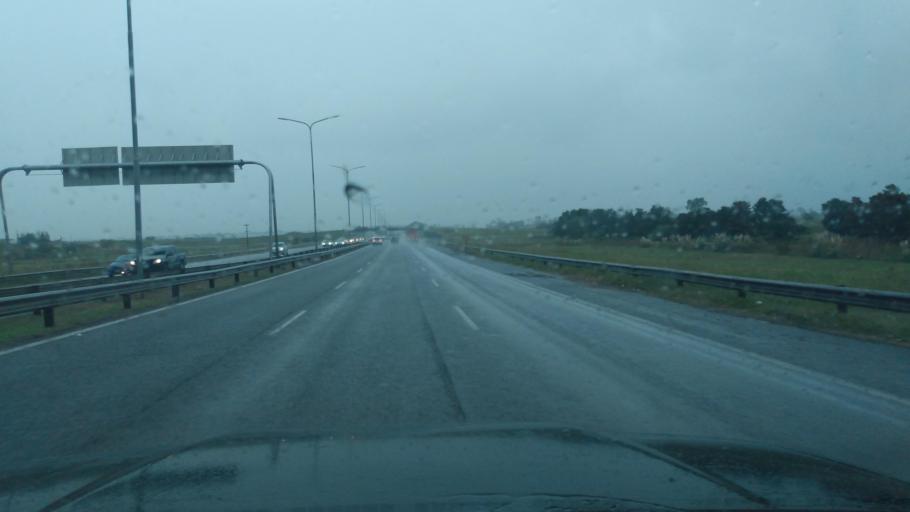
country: AR
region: Buenos Aires
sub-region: Partido de Tigre
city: Tigre
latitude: -34.5128
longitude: -58.5905
